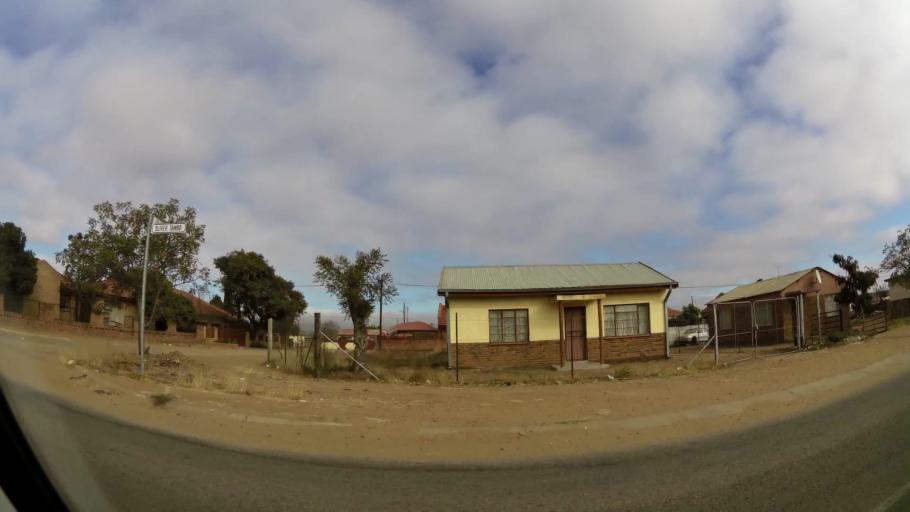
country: ZA
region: Limpopo
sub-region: Capricorn District Municipality
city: Polokwane
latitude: -23.8460
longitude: 29.3805
